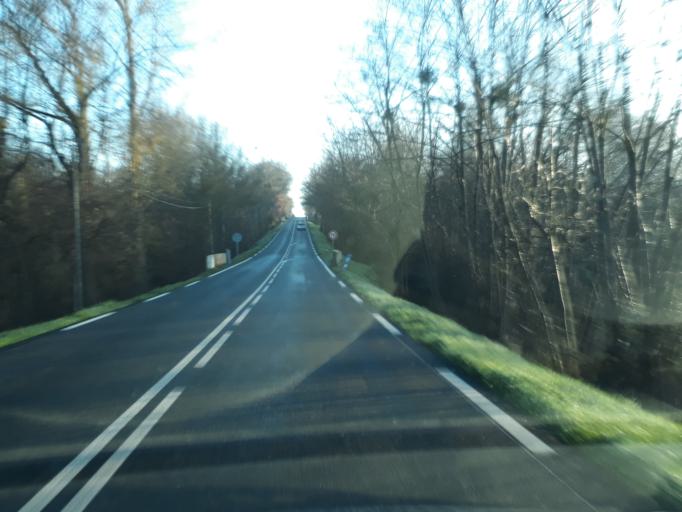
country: FR
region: Midi-Pyrenees
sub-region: Departement de la Haute-Garonne
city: Rieumes
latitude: 43.4182
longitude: 1.1350
